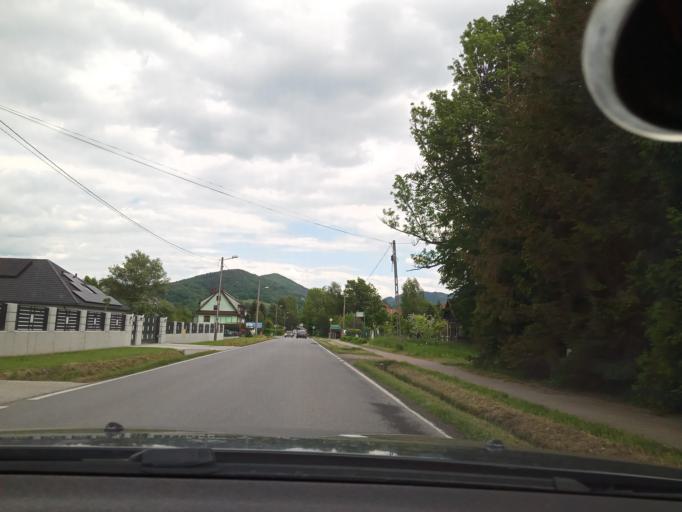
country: PL
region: Lesser Poland Voivodeship
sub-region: Powiat limanowski
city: Limanowa
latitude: 49.7407
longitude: 20.3817
